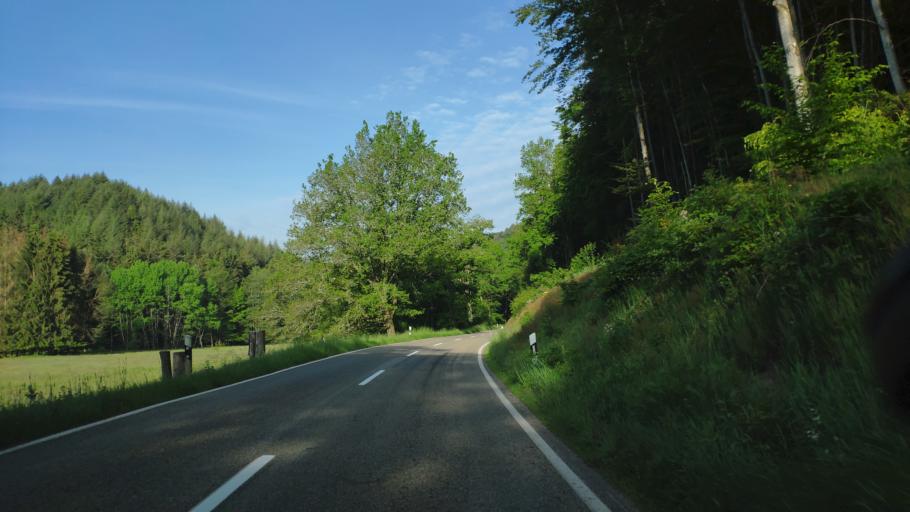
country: DE
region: Rheinland-Pfalz
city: Hinterweidenthal
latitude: 49.1942
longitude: 7.7374
